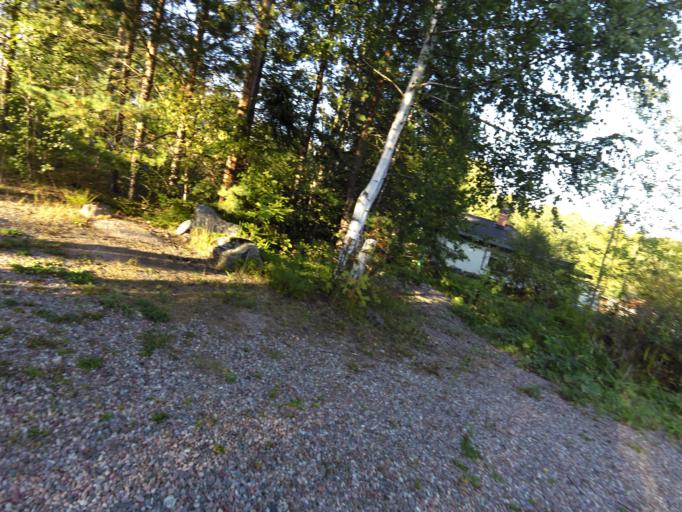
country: SE
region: Gaevleborg
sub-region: Gavle Kommun
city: Gavle
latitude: 60.7096
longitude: 17.1510
